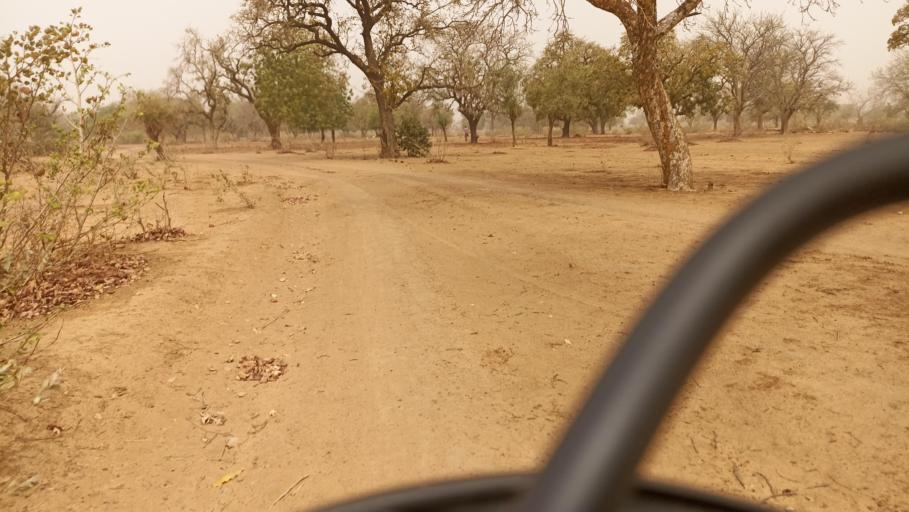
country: BF
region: Nord
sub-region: Province du Zondoma
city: Gourcy
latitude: 13.2512
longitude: -2.6088
